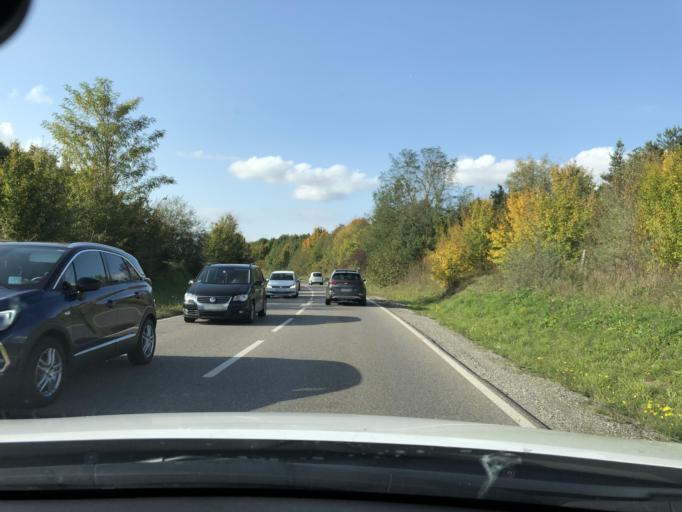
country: DE
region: Bavaria
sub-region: Upper Bavaria
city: Maisach
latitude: 48.2087
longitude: 11.2861
